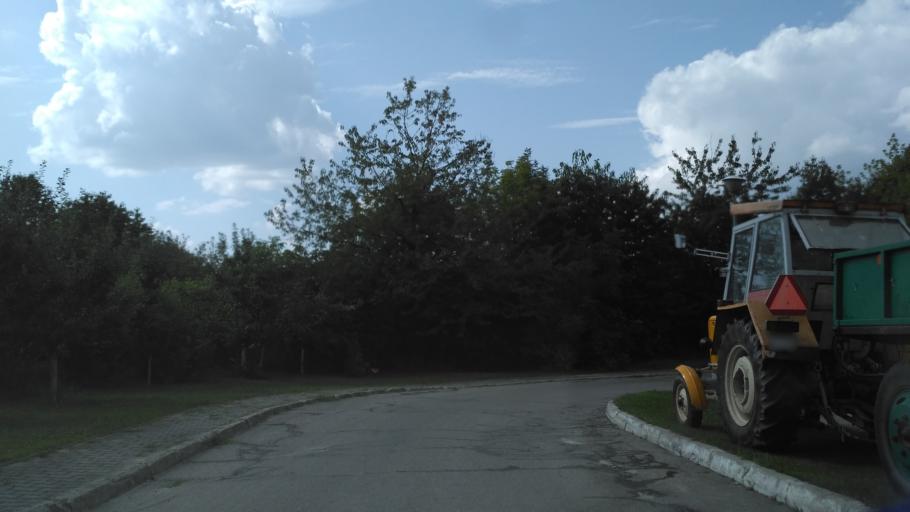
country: PL
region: Lublin Voivodeship
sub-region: Powiat chelmski
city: Rejowiec Fabryczny
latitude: 51.1867
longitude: 23.1665
